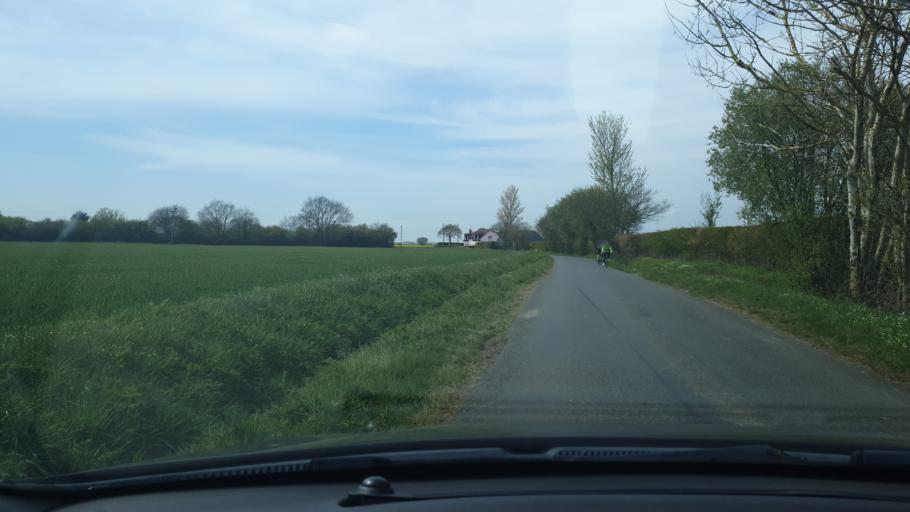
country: GB
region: England
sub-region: Essex
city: Mistley
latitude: 51.8977
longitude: 1.1049
